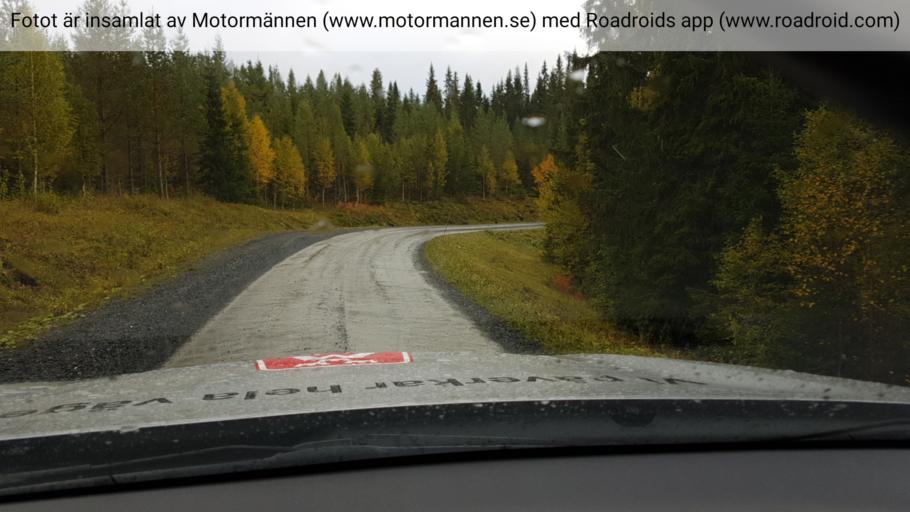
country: SE
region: Jaemtland
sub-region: Krokoms Kommun
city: Valla
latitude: 64.1092
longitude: 14.1494
